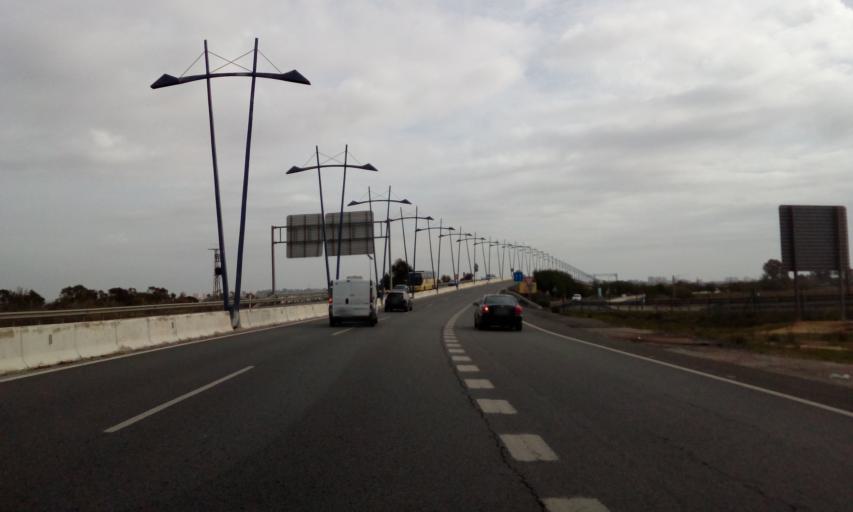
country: ES
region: Andalusia
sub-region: Provincia de Huelva
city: Aljaraque
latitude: 37.2717
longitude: -6.9864
